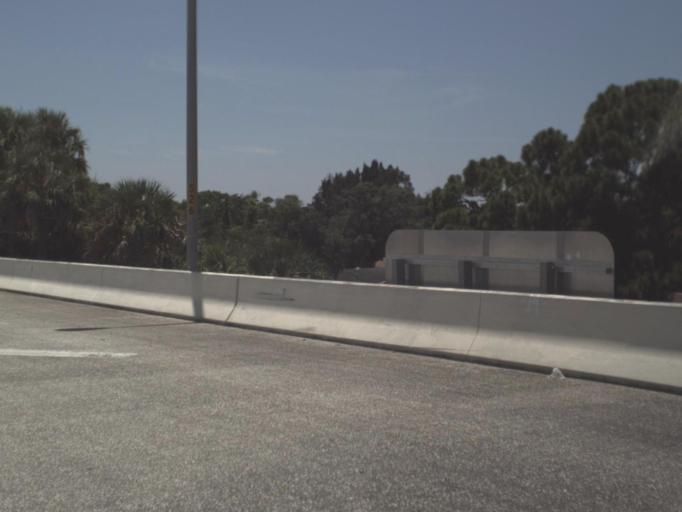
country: US
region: Florida
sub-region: Pinellas County
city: Saint Petersburg
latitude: 27.7484
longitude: -82.6775
